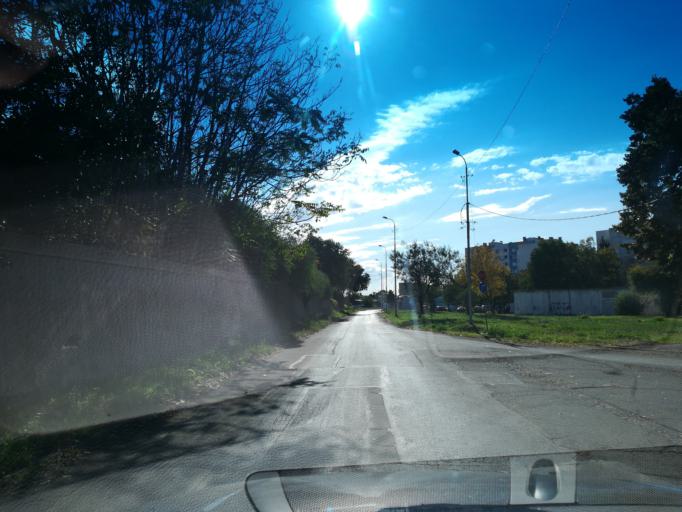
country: BG
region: Stara Zagora
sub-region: Obshtina Stara Zagora
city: Stara Zagora
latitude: 42.4259
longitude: 25.6467
